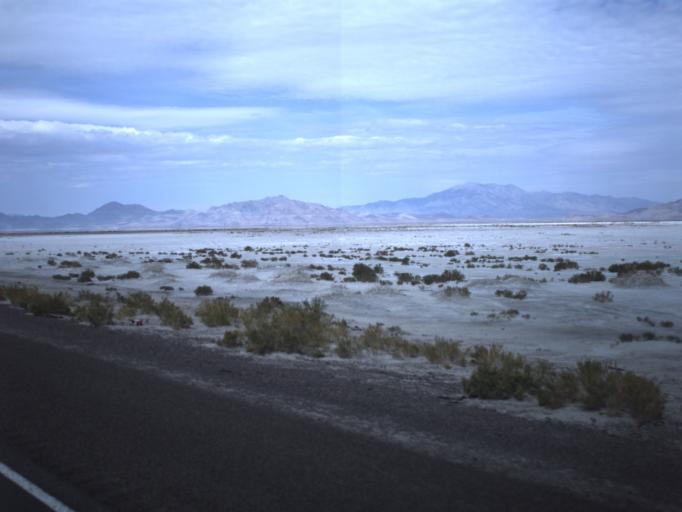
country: US
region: Utah
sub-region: Tooele County
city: Wendover
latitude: 40.7368
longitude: -113.7269
